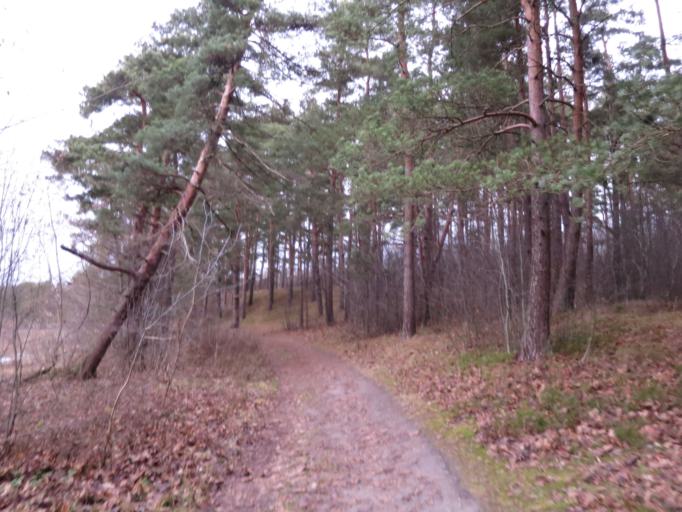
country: LV
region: Riga
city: Bergi
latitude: 56.9753
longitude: 24.3065
